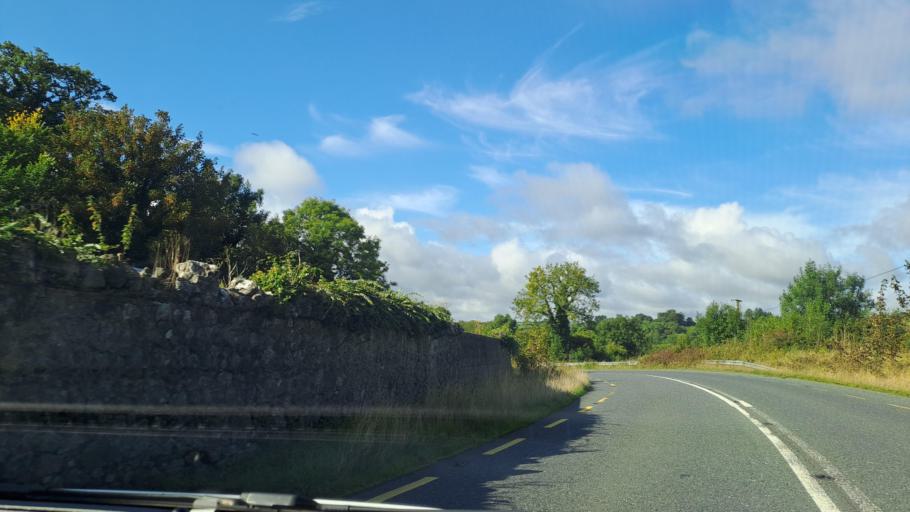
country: IE
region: Ulster
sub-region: County Monaghan
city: Carrickmacross
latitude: 53.9724
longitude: -6.7400
